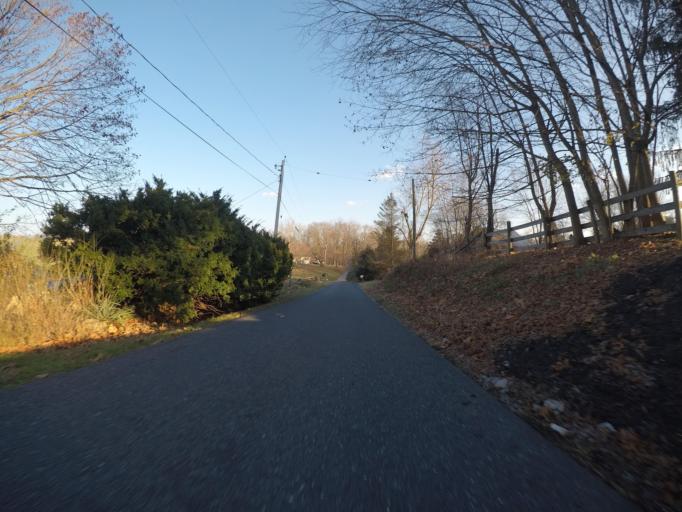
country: US
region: Maryland
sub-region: Carroll County
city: Hampstead
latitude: 39.5367
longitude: -76.8776
